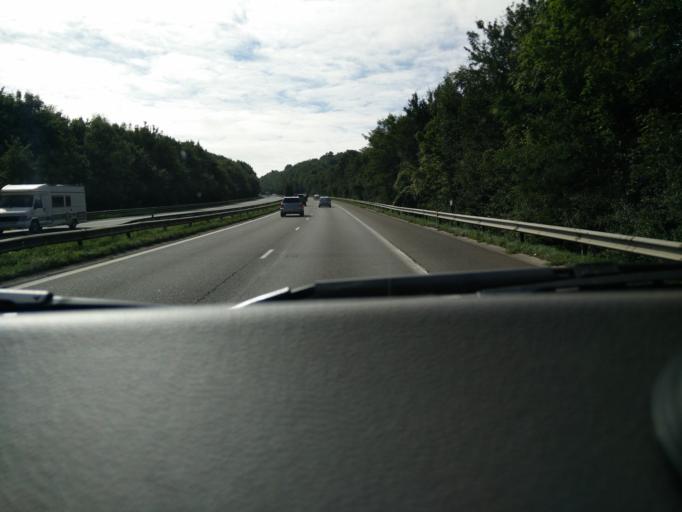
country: BE
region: Wallonia
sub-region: Province de Namur
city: Houyet
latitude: 50.2358
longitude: 5.0504
